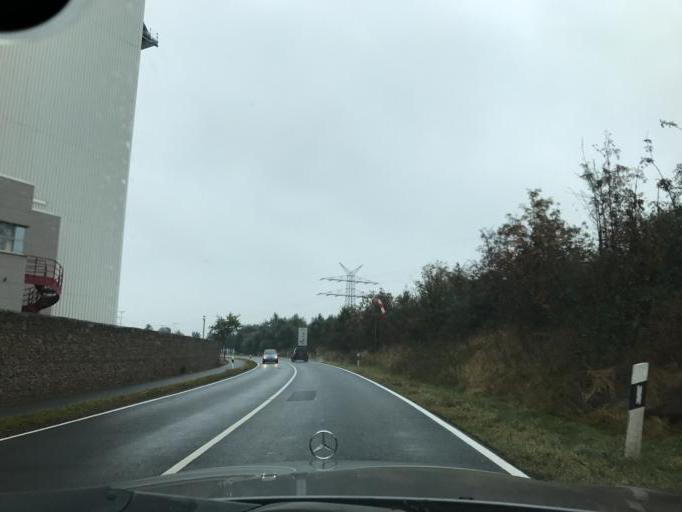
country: DE
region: Lower Saxony
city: Papenburg
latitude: 53.0942
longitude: 7.3557
